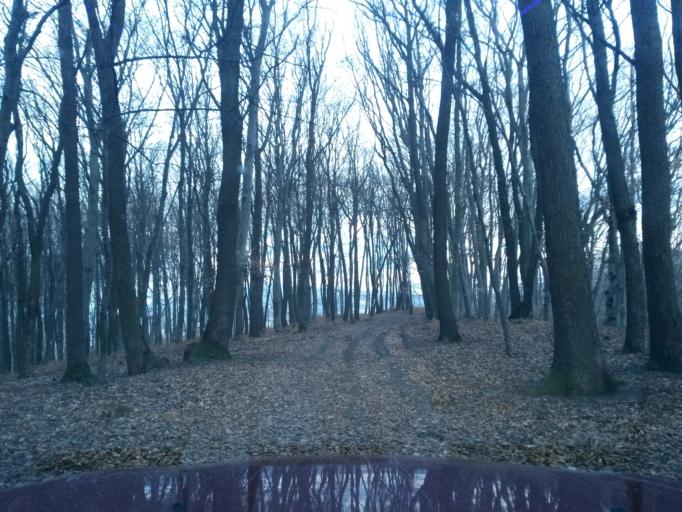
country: SK
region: Kosicky
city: Kosice
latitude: 48.7027
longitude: 21.3811
